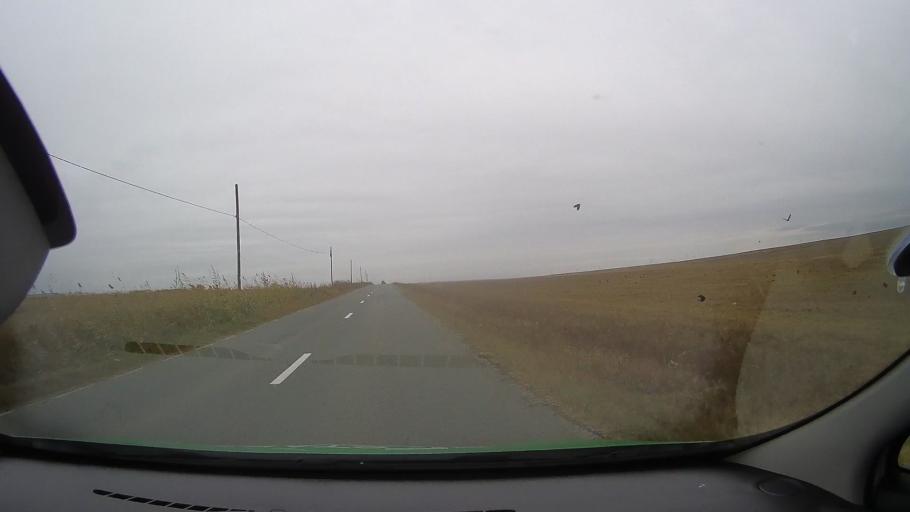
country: RO
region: Constanta
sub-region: Comuna Silistea
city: Silistea
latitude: 44.4375
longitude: 28.2258
